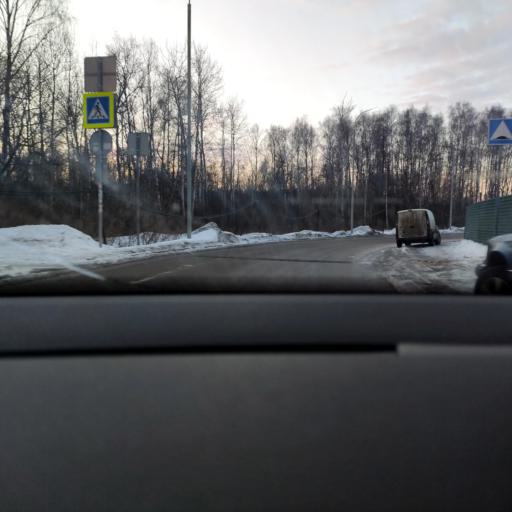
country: RU
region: Moskovskaya
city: Oktyabr'skiy
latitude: 55.6022
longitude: 37.9893
